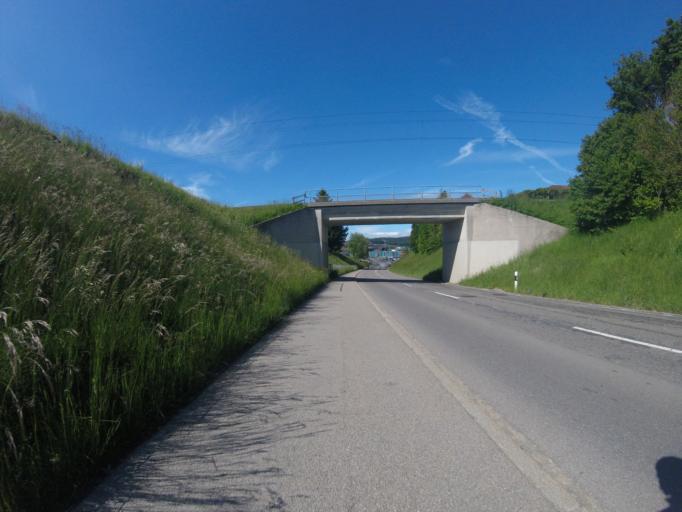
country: CH
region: Saint Gallen
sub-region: Wahlkreis Wil
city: Wil
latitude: 47.4437
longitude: 9.0503
